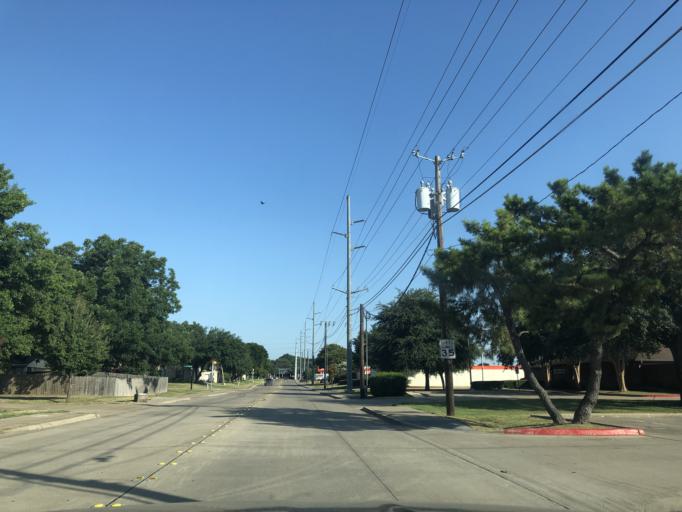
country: US
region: Texas
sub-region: Dallas County
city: Garland
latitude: 32.8662
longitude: -96.6312
